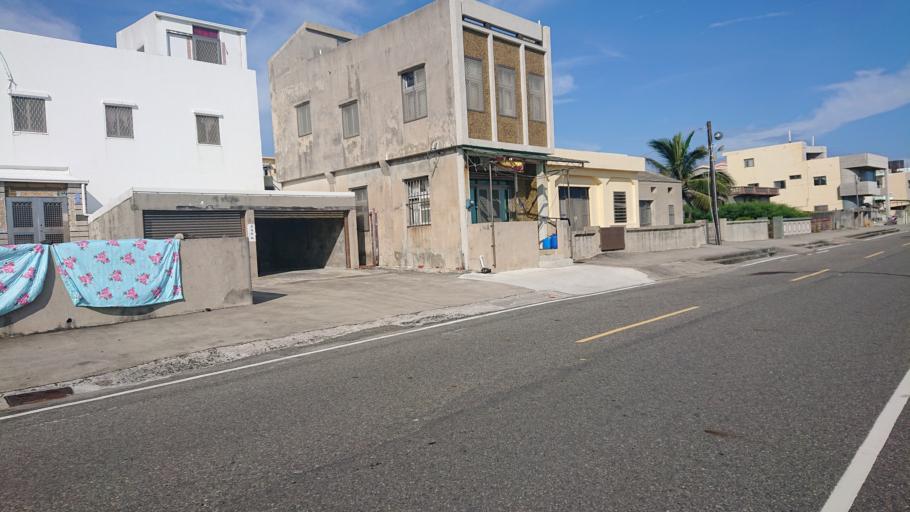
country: TW
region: Taiwan
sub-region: Penghu
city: Ma-kung
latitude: 23.5241
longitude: 119.5706
